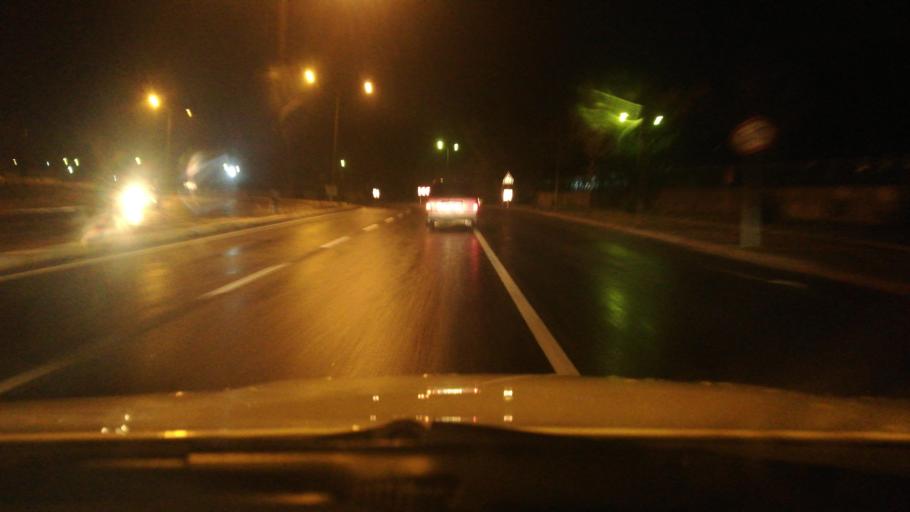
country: TR
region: Kahramanmaras
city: Kahramanmaras
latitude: 37.5985
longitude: 36.9255
